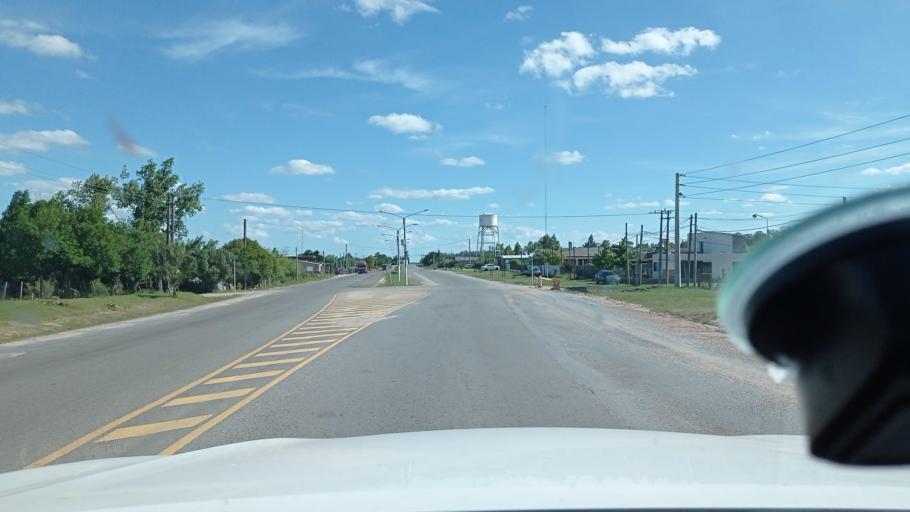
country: UY
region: Florida
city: Florida
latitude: -34.0847
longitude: -56.2369
